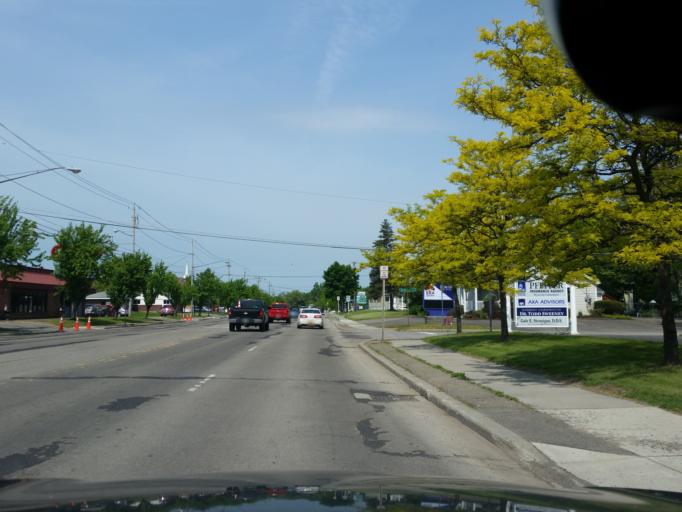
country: US
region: New York
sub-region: Chautauqua County
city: Celoron
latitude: 42.0979
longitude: -79.2956
